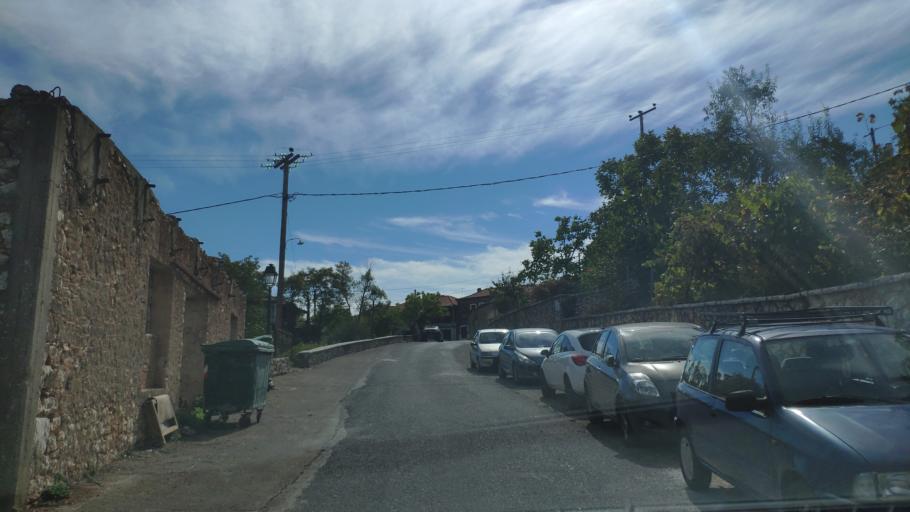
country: GR
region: Peloponnese
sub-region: Nomos Arkadias
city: Dimitsana
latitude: 37.5216
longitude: 22.0720
